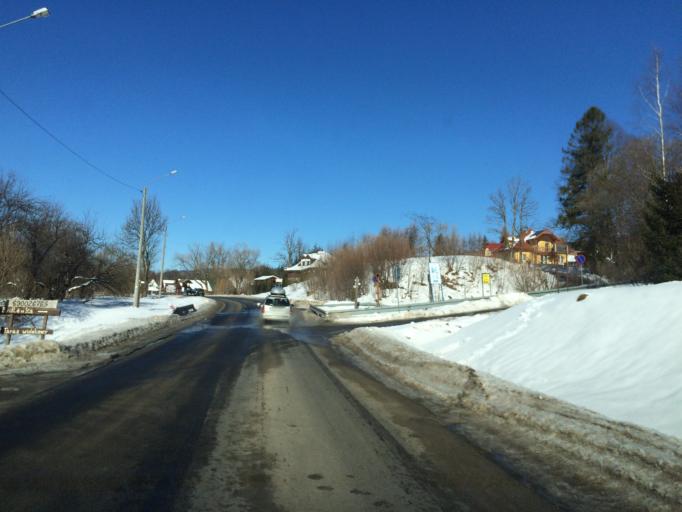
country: PL
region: Subcarpathian Voivodeship
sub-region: Powiat leski
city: Cisna
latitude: 49.1589
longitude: 22.4637
